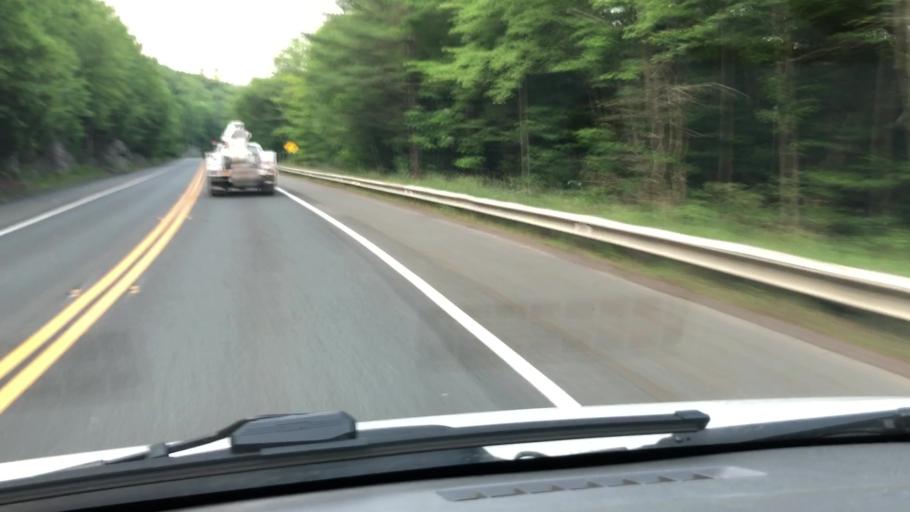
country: US
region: Massachusetts
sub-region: Hampshire County
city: Chesterfield
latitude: 42.4525
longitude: -72.8556
